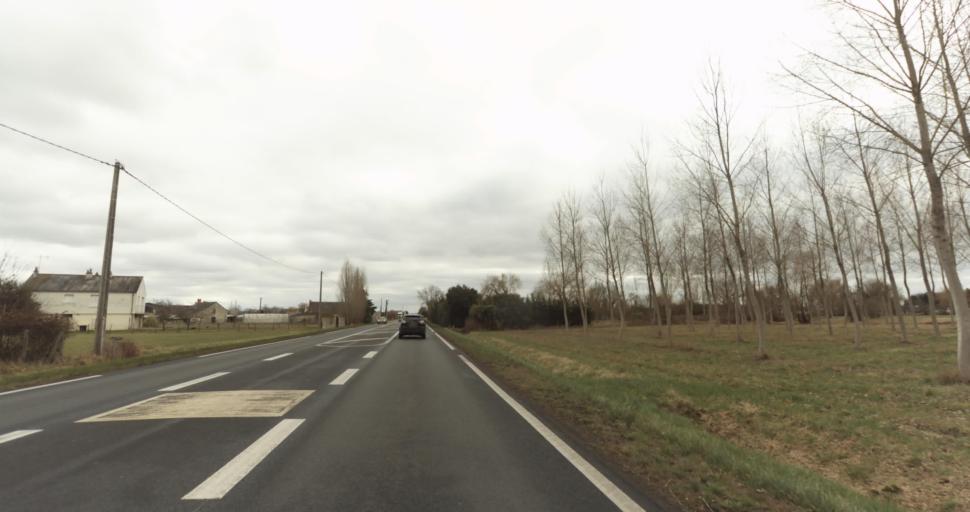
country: FR
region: Pays de la Loire
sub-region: Departement de Maine-et-Loire
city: Vivy
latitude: 47.3194
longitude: -0.0498
